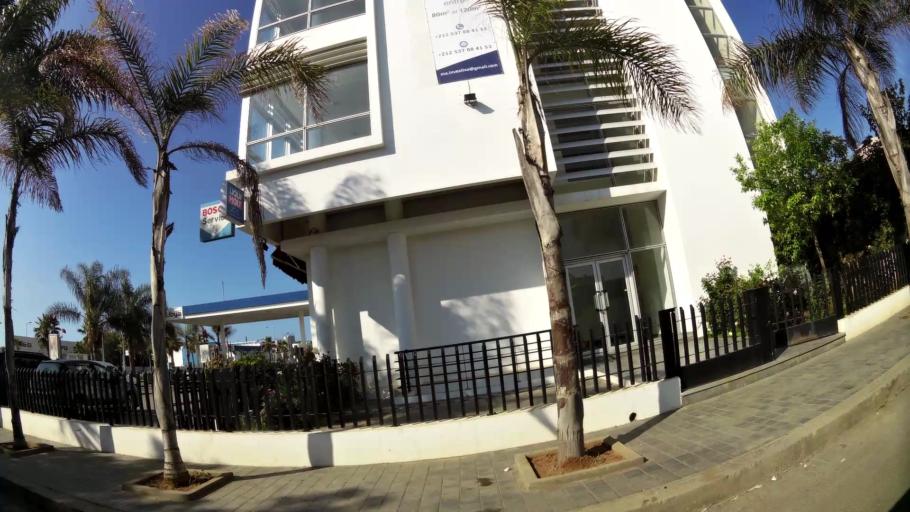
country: MA
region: Rabat-Sale-Zemmour-Zaer
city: Sale
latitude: 34.0531
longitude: -6.8102
